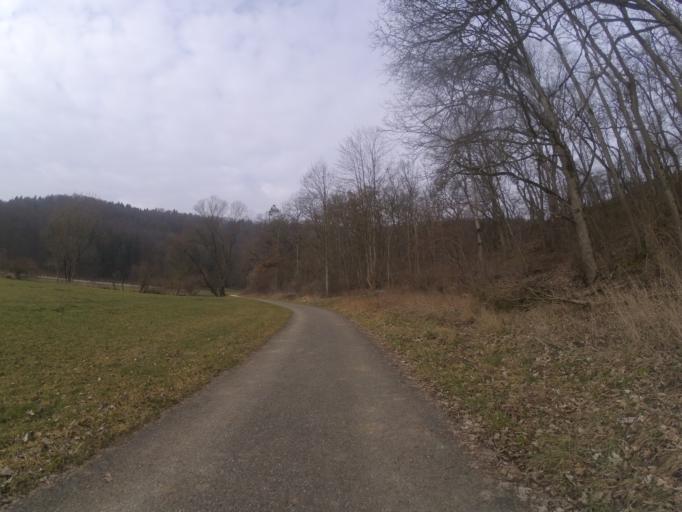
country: DE
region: Baden-Wuerttemberg
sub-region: Tuebingen Region
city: Hayingen
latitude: 48.2976
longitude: 9.4935
